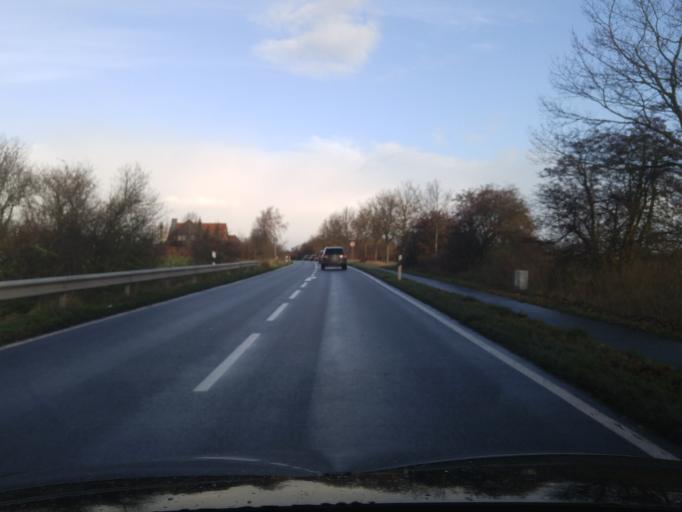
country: DE
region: Schleswig-Holstein
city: Timmendorfer Strand
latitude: 53.9825
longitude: 10.7727
